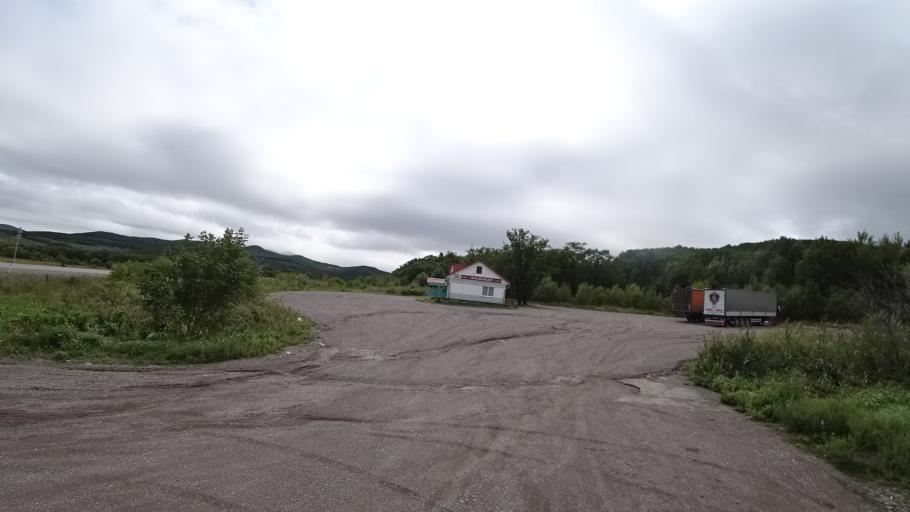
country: RU
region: Primorskiy
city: Monastyrishche
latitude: 44.1643
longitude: 132.4396
